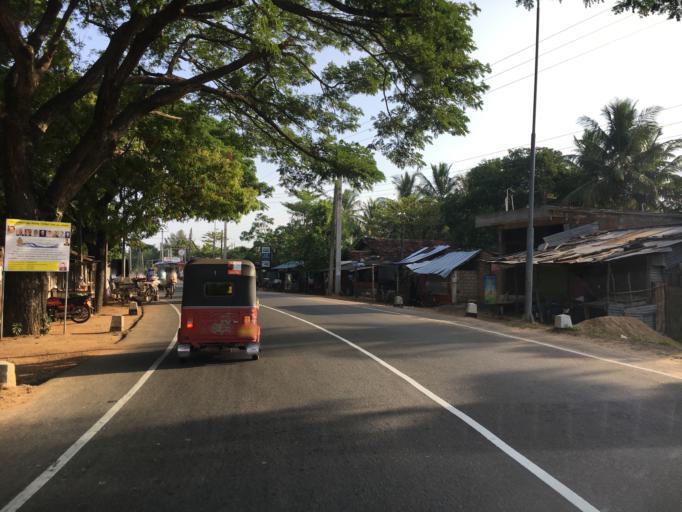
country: LK
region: Eastern Province
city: Eravur Town
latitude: 7.9239
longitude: 81.5137
